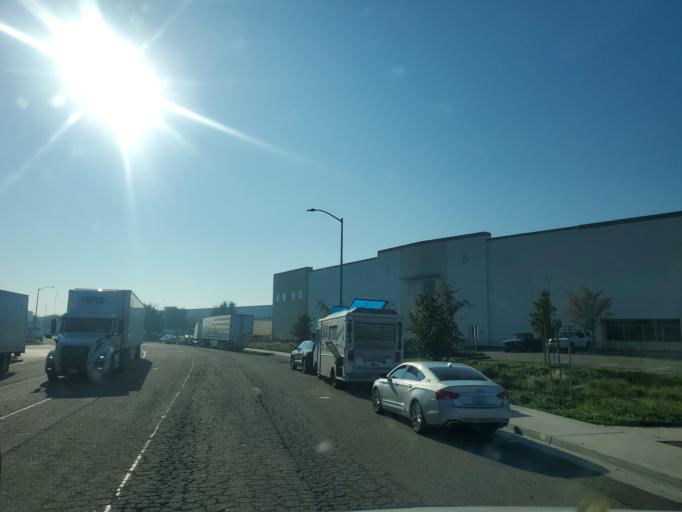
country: US
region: California
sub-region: San Joaquin County
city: French Camp
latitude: 37.8969
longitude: -121.2611
